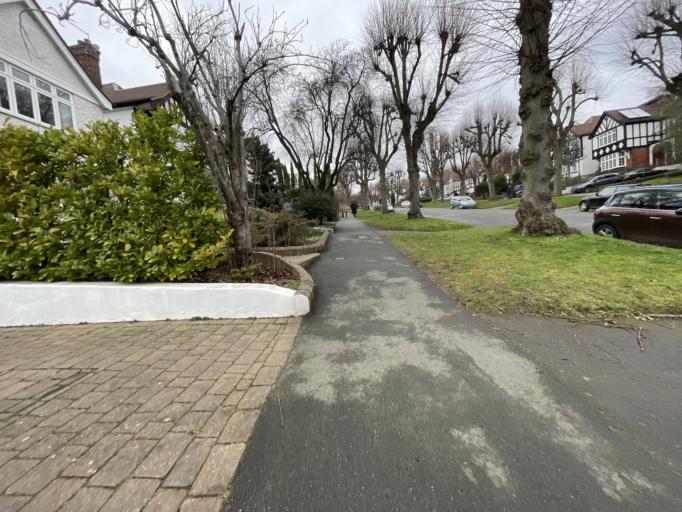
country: GB
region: England
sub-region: Greater London
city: Camden Town
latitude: 51.5649
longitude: -0.1497
